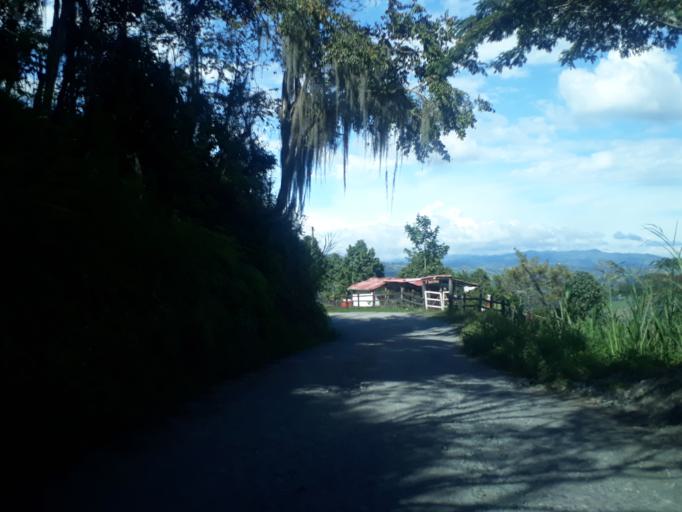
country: CO
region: Santander
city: Velez
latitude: 6.0354
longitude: -73.6530
